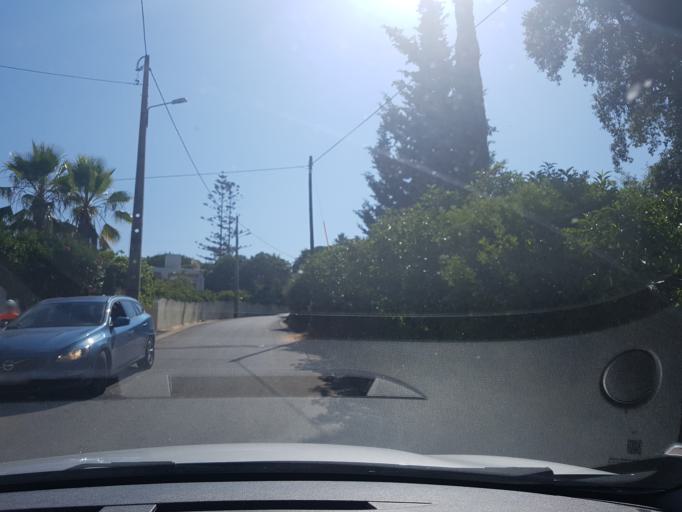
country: PT
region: Faro
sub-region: Lagoa
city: Carvoeiro
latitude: 37.0990
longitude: -8.4592
